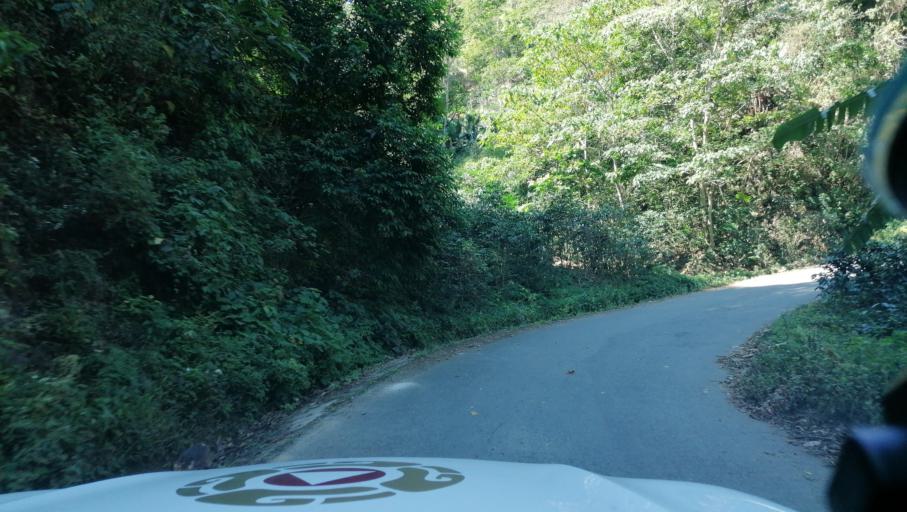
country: MX
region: Chiapas
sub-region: Cacahoatan
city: Benito Juarez
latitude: 15.1805
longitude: -92.1888
